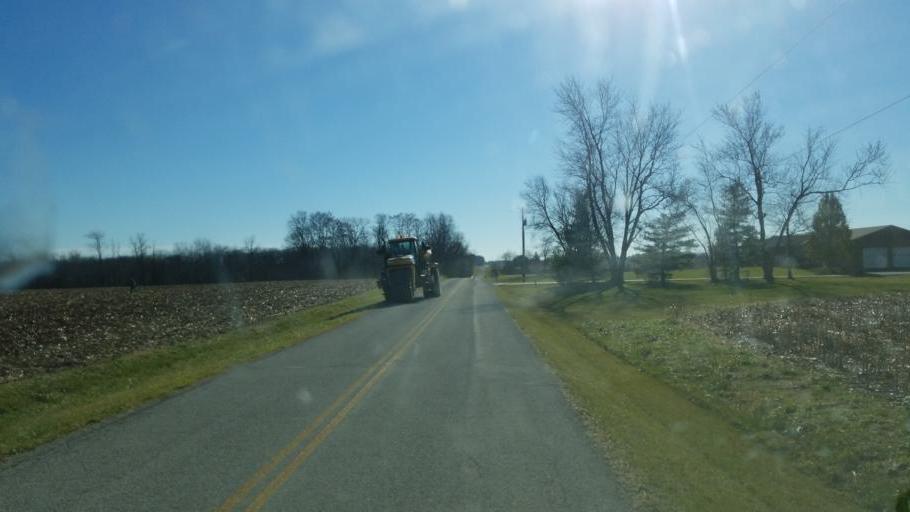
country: US
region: Ohio
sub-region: Crawford County
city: Crestline
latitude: 40.8464
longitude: -82.8371
